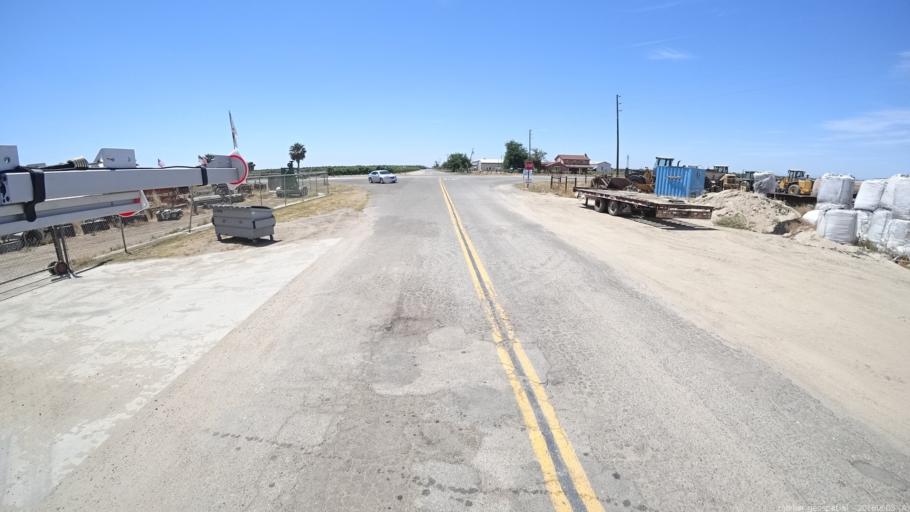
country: US
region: California
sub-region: Madera County
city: Chowchilla
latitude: 37.0841
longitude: -120.4189
